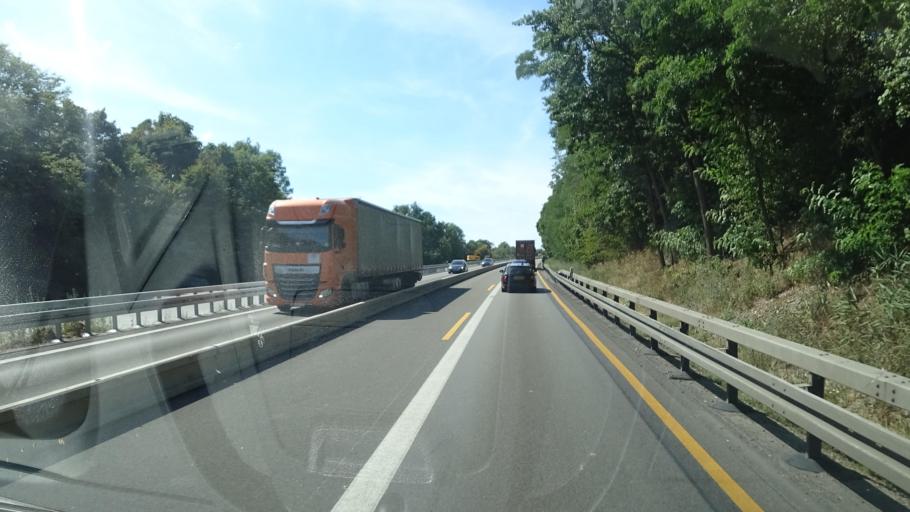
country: DE
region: Brandenburg
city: Frankfurt (Oder)
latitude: 52.3146
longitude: 14.5405
